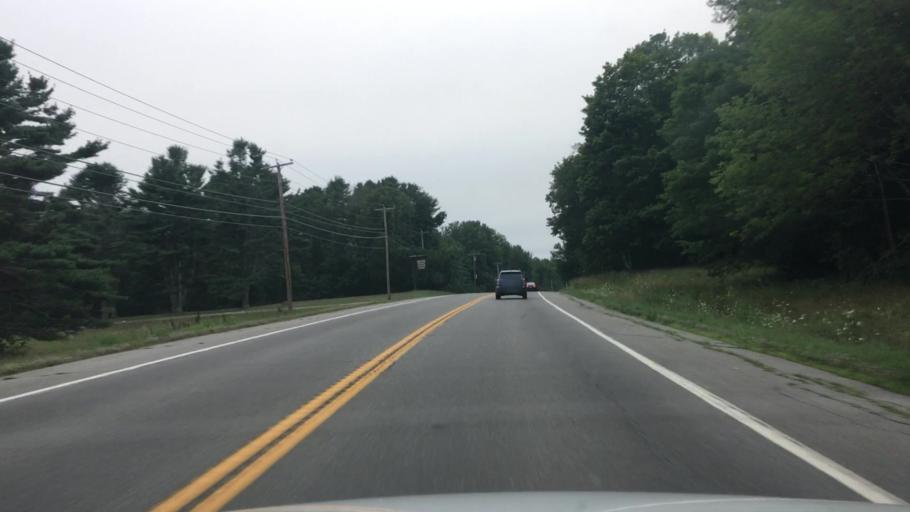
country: US
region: Maine
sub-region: Waldo County
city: Belfast
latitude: 44.4357
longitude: -68.9440
